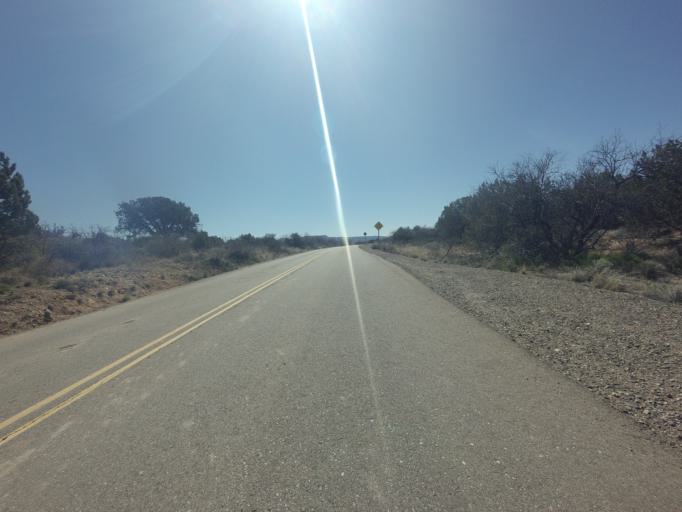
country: US
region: Arizona
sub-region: Yavapai County
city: Lake Montezuma
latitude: 34.6863
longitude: -111.7373
